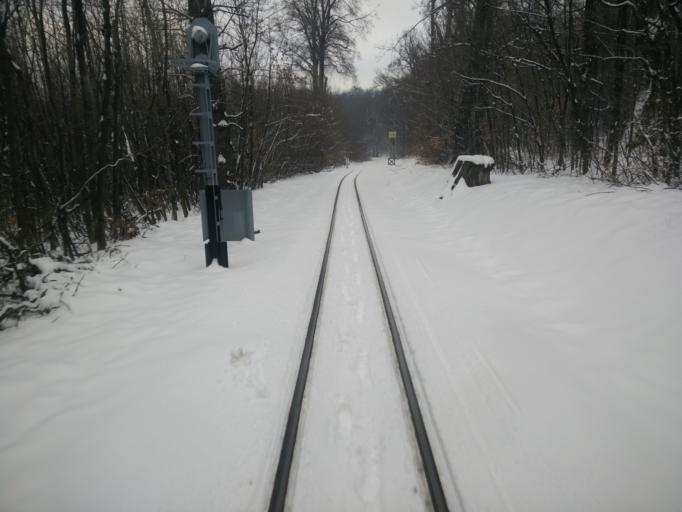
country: HU
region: Pest
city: Budakeszi
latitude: 47.5016
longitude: 18.9606
